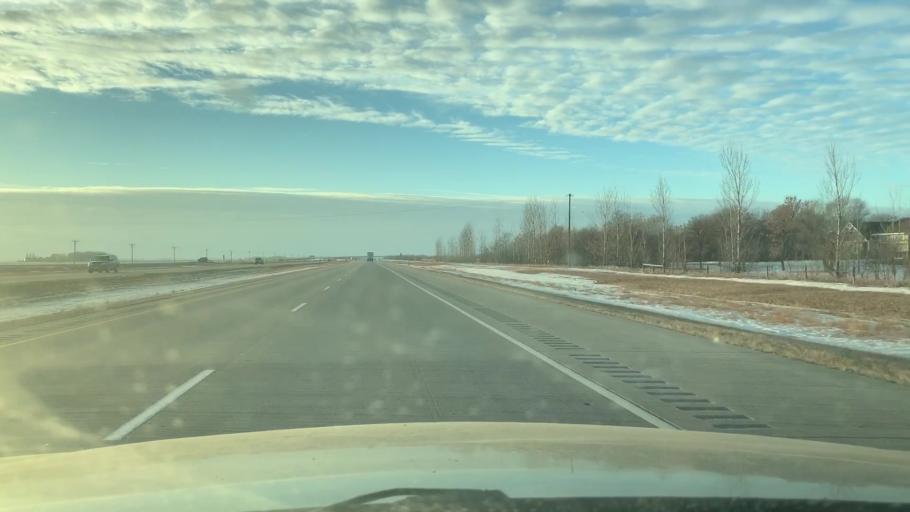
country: US
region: North Dakota
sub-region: Cass County
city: Casselton
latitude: 46.8766
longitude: -97.3179
